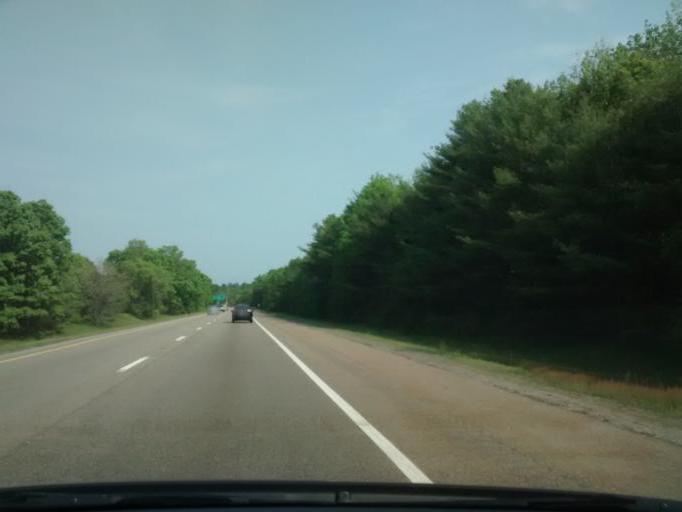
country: US
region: Massachusetts
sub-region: Plymouth County
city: West Wareham
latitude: 41.7876
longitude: -70.7407
